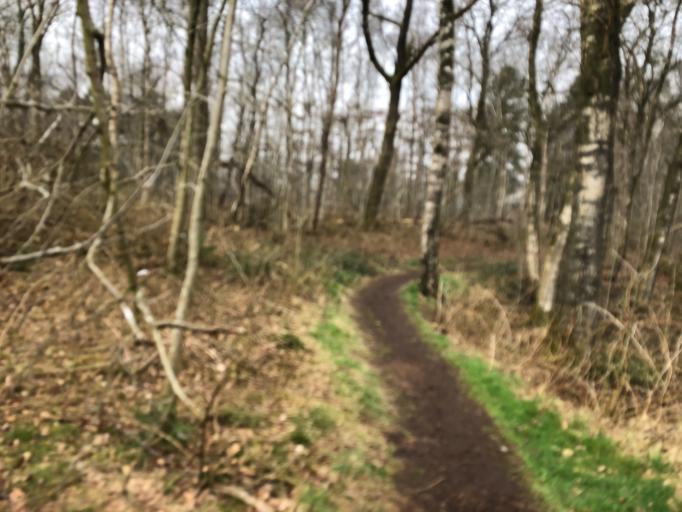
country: DE
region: Schleswig-Holstein
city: Wanderup
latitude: 54.6887
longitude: 9.3429
